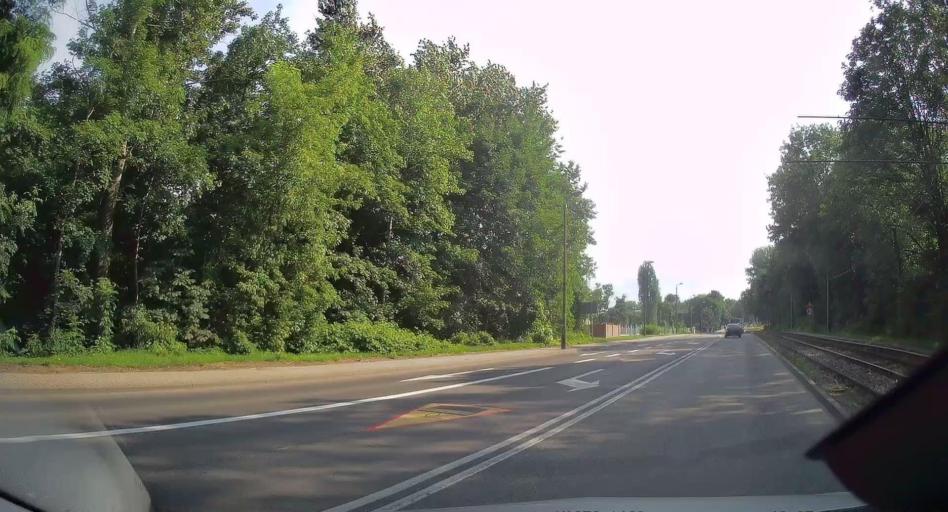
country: PL
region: Silesian Voivodeship
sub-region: Swietochlowice
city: Swietochlowice
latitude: 50.3079
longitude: 18.9219
